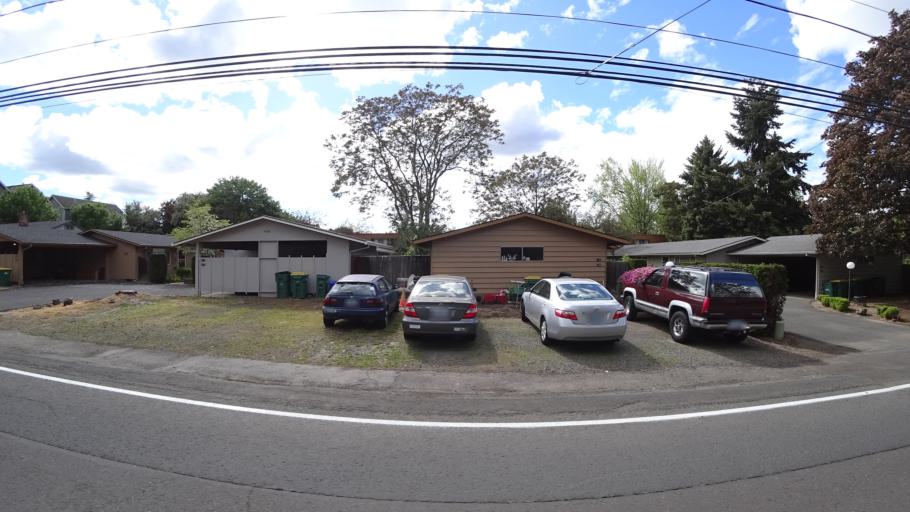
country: US
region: Oregon
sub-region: Washington County
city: Beaverton
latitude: 45.4825
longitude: -122.8171
